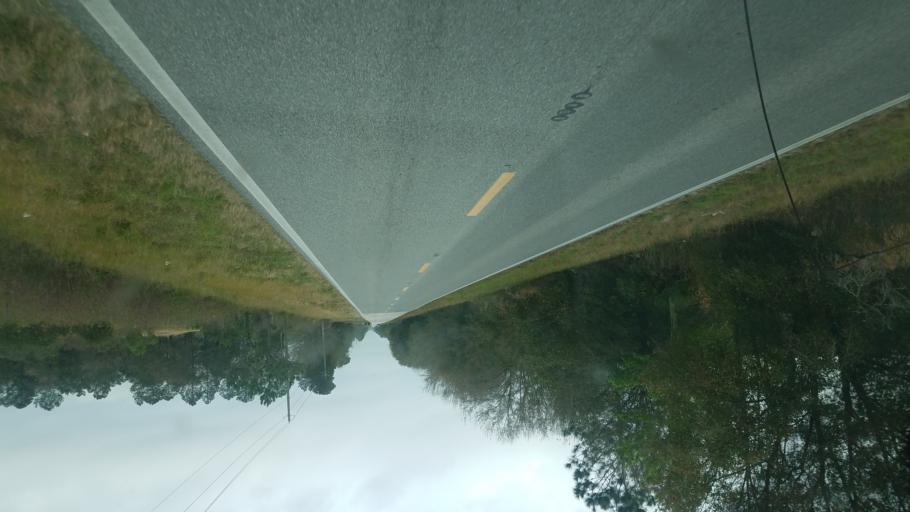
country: US
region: Florida
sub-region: Polk County
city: Polk City
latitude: 28.2589
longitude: -81.9137
